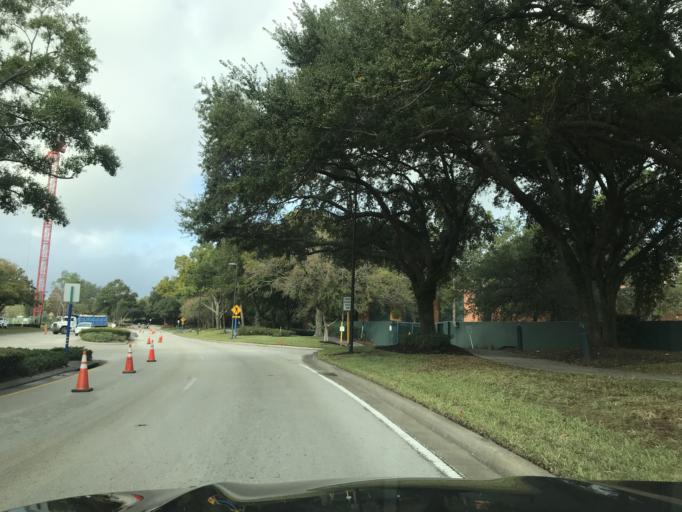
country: US
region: Florida
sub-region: Osceola County
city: Celebration
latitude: 28.3644
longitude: -81.5597
